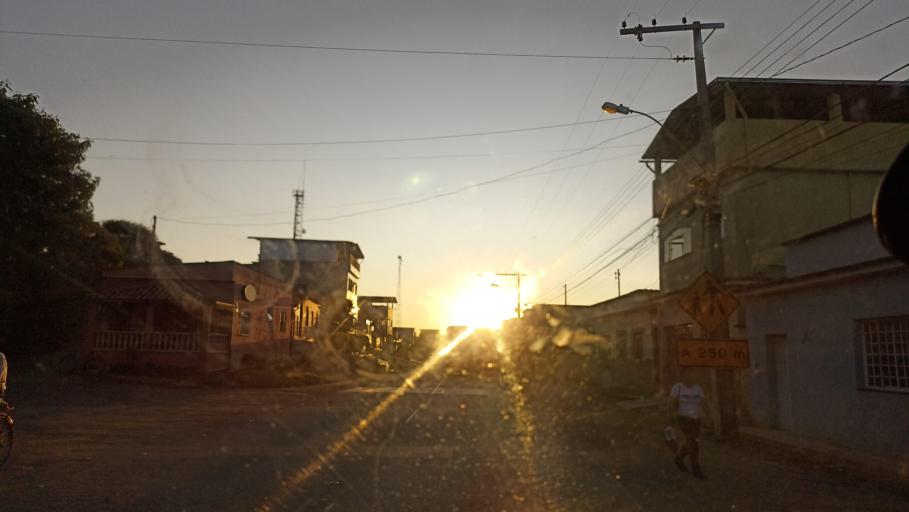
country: BR
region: Minas Gerais
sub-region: Sao Joao Del Rei
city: Sao Joao del Rei
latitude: -21.2438
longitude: -44.4101
